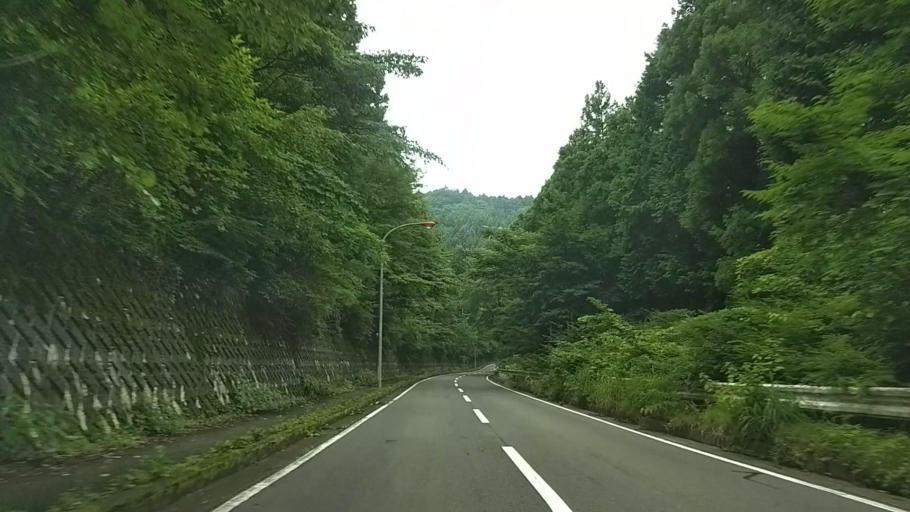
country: JP
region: Shizuoka
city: Gotemba
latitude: 35.3209
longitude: 139.0427
